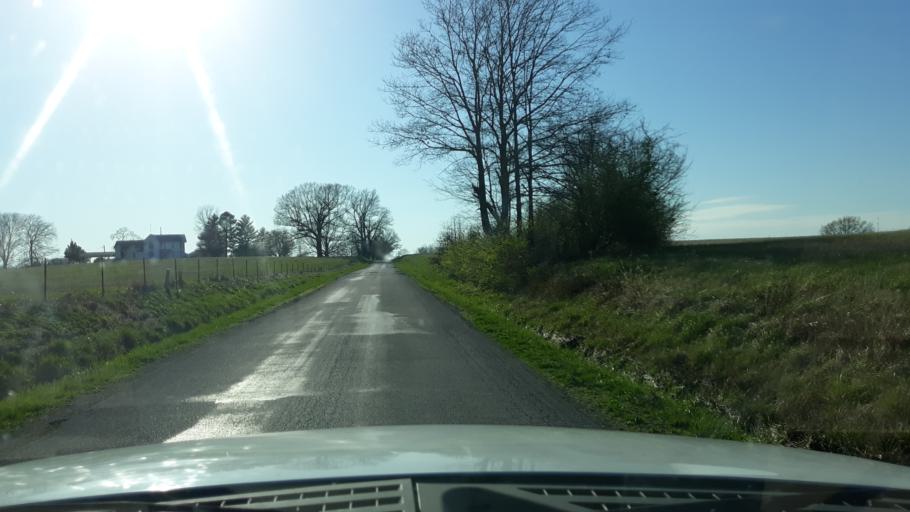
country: US
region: Illinois
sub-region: Saline County
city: Harrisburg
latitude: 37.7645
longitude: -88.5831
